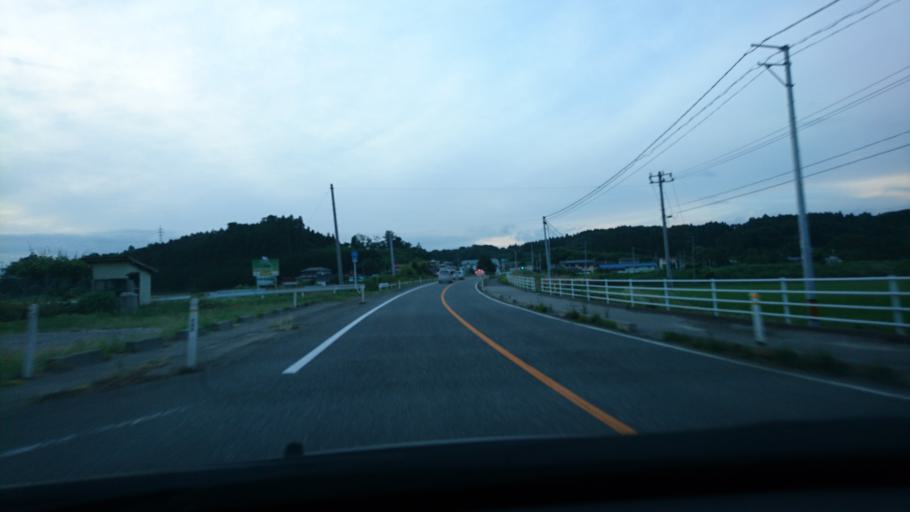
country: JP
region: Iwate
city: Ichinoseki
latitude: 38.7698
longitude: 141.0002
